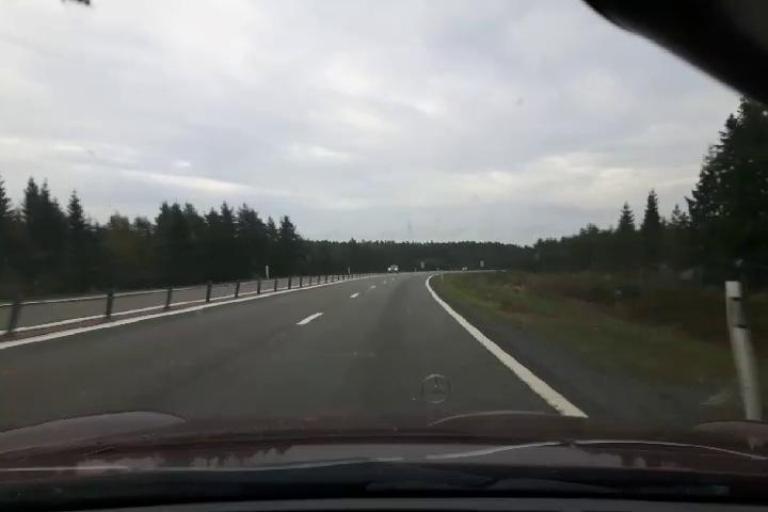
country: SE
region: Vaesternorrland
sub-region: Haernoesands Kommun
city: Haernoesand
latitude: 62.7242
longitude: 17.9221
